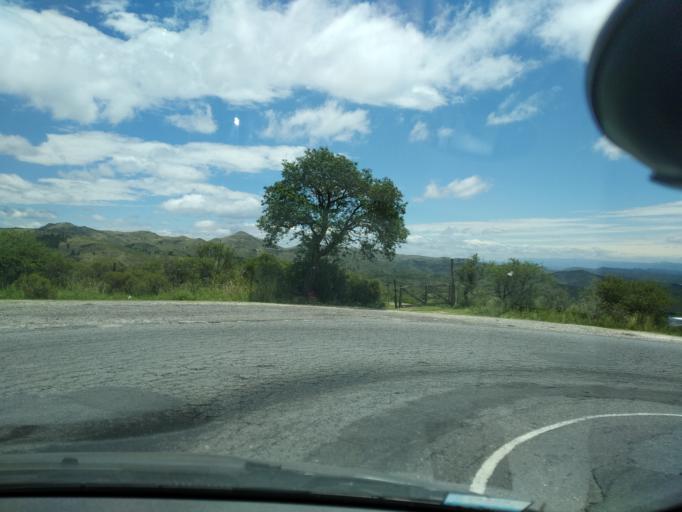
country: AR
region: Cordoba
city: Cuesta Blanca
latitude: -31.5939
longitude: -64.5324
